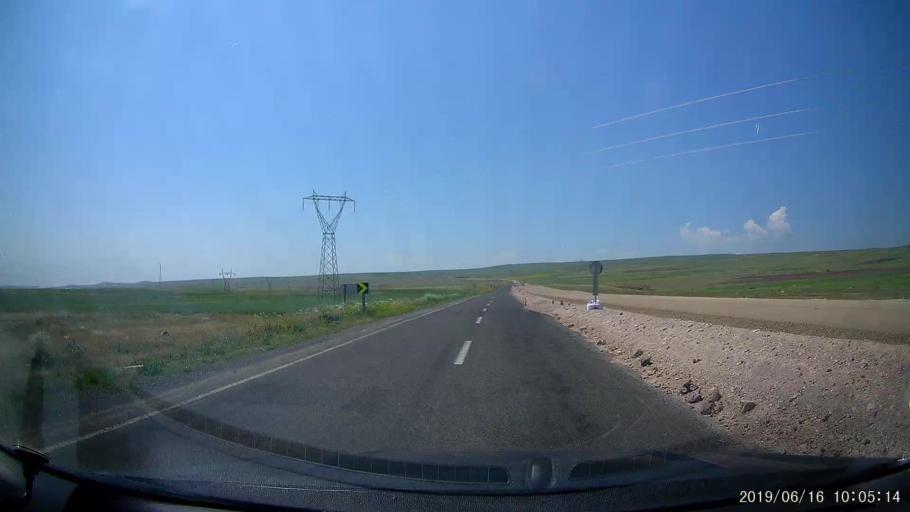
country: TR
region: Kars
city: Digor
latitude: 40.2730
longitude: 43.5378
